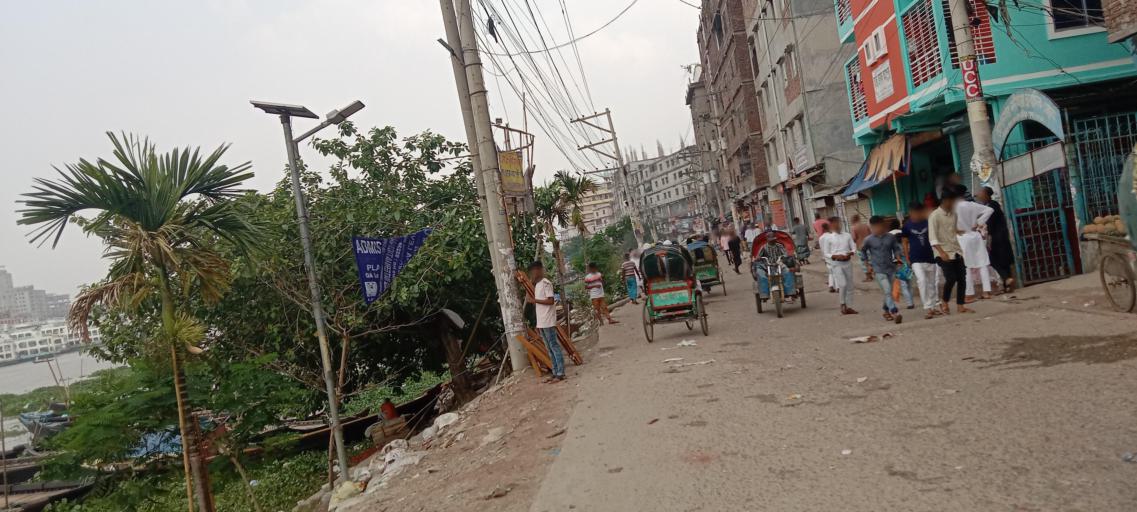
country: BD
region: Dhaka
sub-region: Dhaka
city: Dhaka
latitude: 23.7061
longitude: 90.4038
